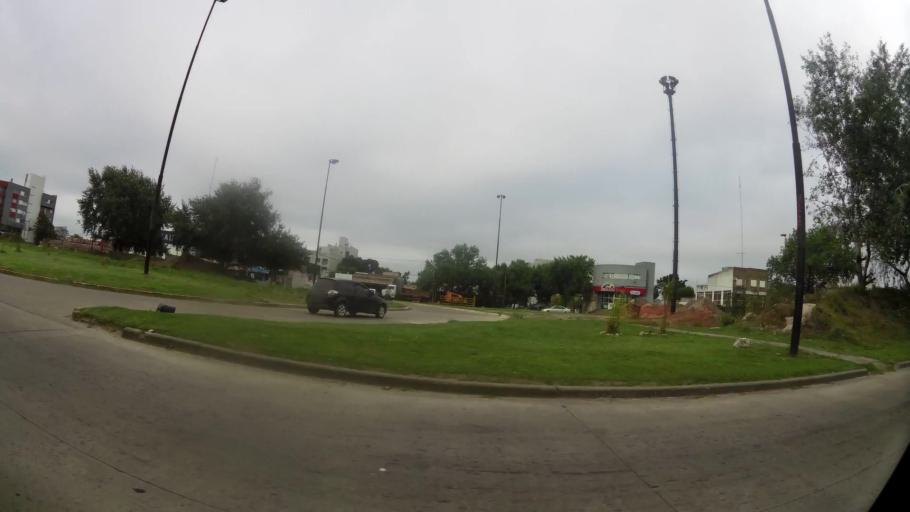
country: AR
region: Buenos Aires
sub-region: Partido de La Plata
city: La Plata
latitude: -34.9294
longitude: -57.9868
